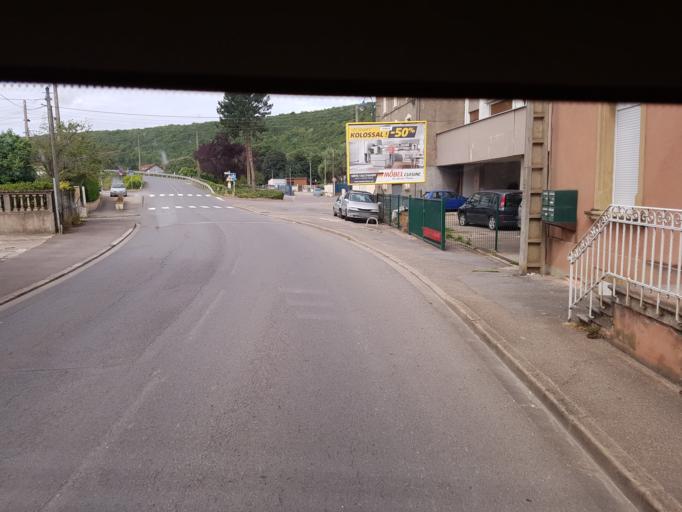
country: FR
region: Lorraine
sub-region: Departement de la Moselle
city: Moyeuvre-Grande
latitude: 49.2481
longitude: 6.0396
